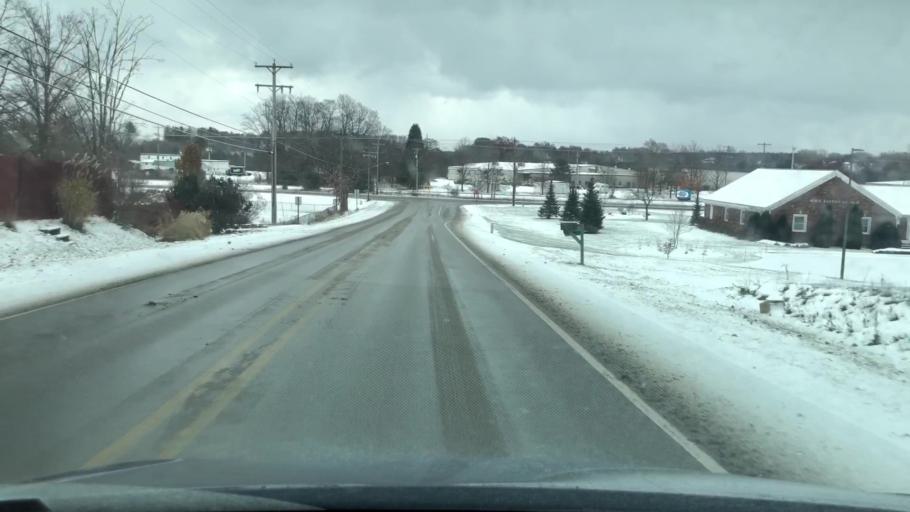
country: US
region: Michigan
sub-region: Grand Traverse County
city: Traverse City
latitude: 44.7154
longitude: -85.6281
